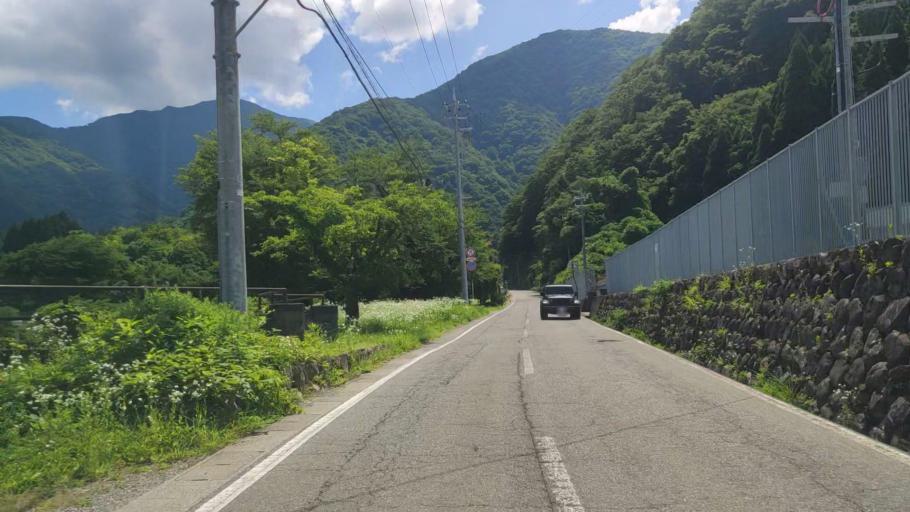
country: JP
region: Fukui
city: Ono
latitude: 35.9358
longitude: 136.5554
